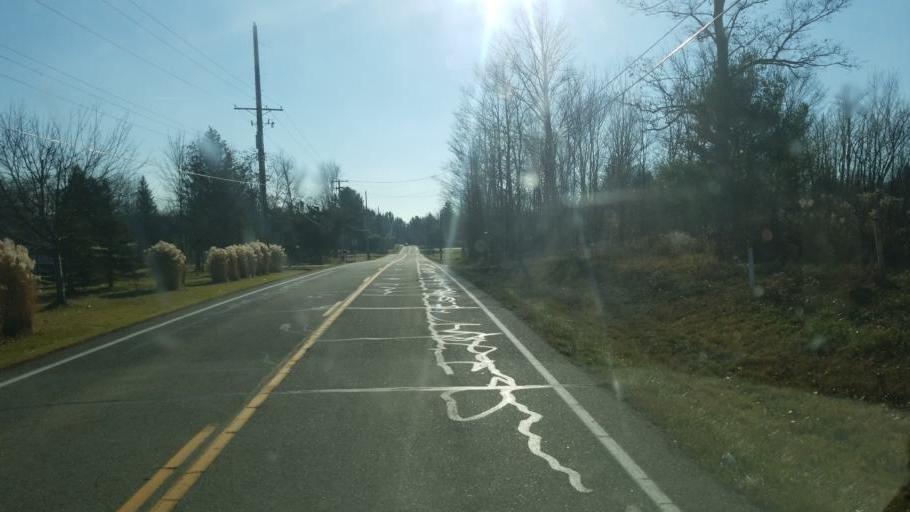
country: US
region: Ohio
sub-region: Geauga County
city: Burton
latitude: 41.4399
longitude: -81.2470
